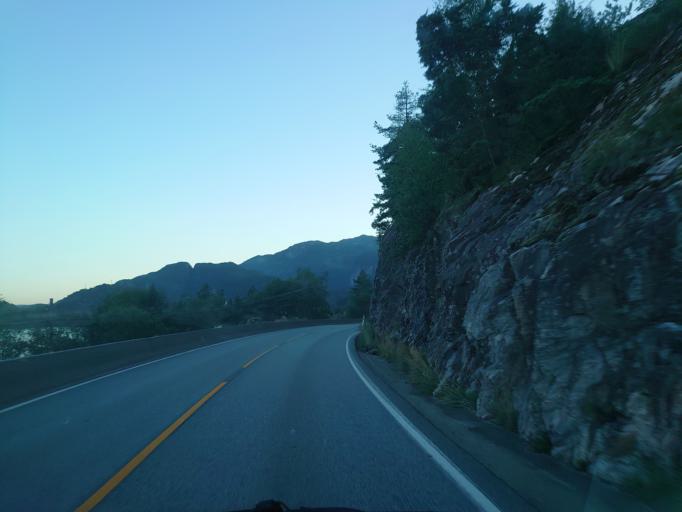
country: NO
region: Hordaland
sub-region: Osteroy
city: Lonevag
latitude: 60.7042
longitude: 5.6056
